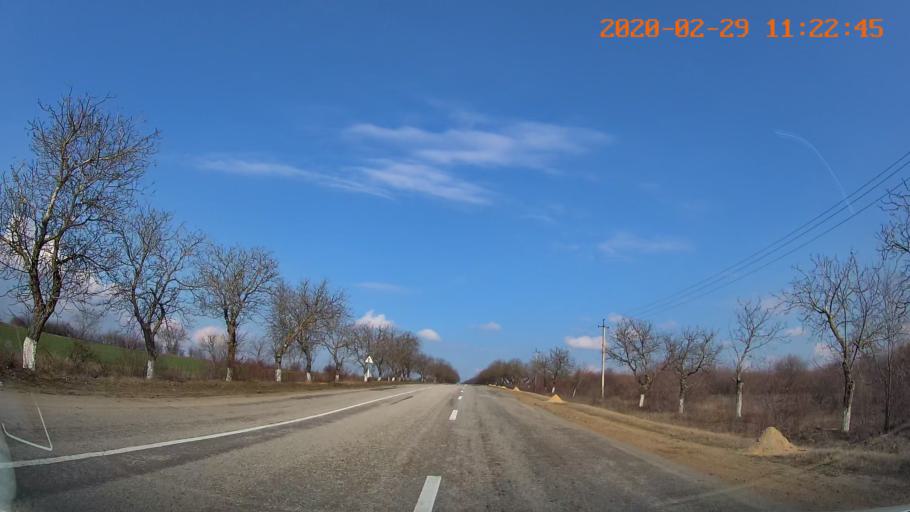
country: MD
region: Telenesti
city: Cocieri
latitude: 47.3983
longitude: 29.1611
